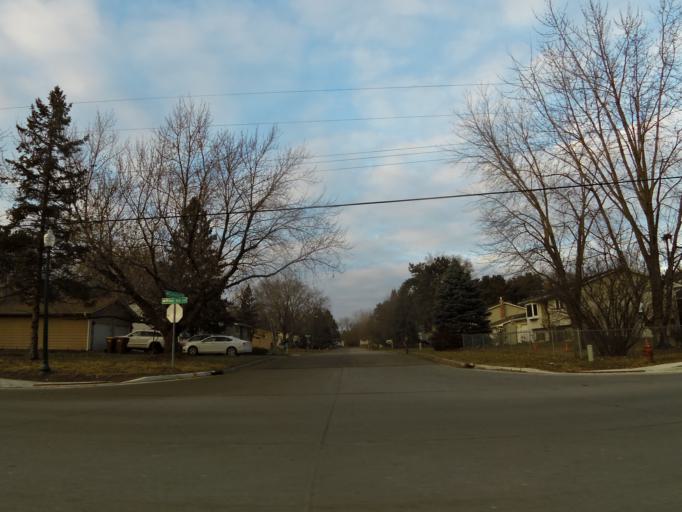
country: US
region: Minnesota
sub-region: Ramsey County
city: White Bear Lake
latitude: 45.0792
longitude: -93.0314
